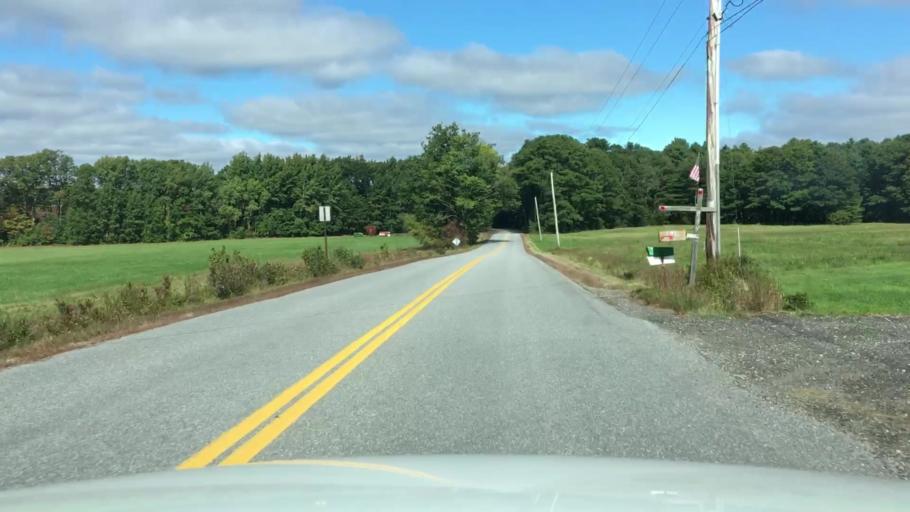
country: US
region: Maine
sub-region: Cumberland County
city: Brunswick
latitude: 43.9503
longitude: -69.8941
